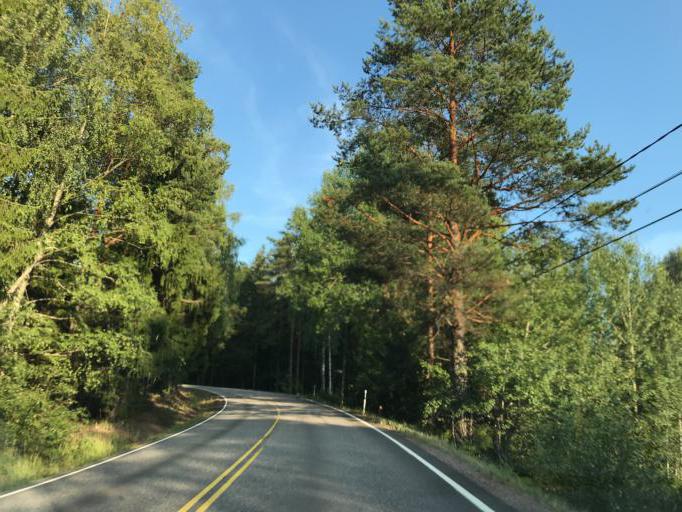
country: FI
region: Uusimaa
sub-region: Helsinki
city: Vihti
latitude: 60.4167
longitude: 24.4119
